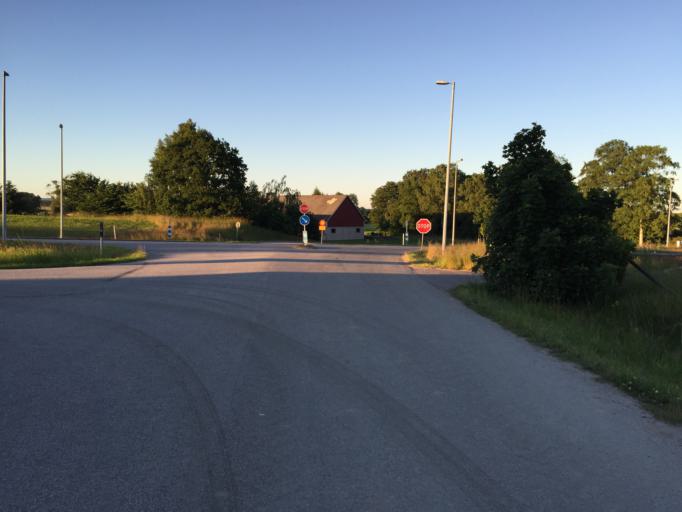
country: SE
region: Skane
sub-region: Lunds Kommun
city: Veberod
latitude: 55.6439
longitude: 13.4720
